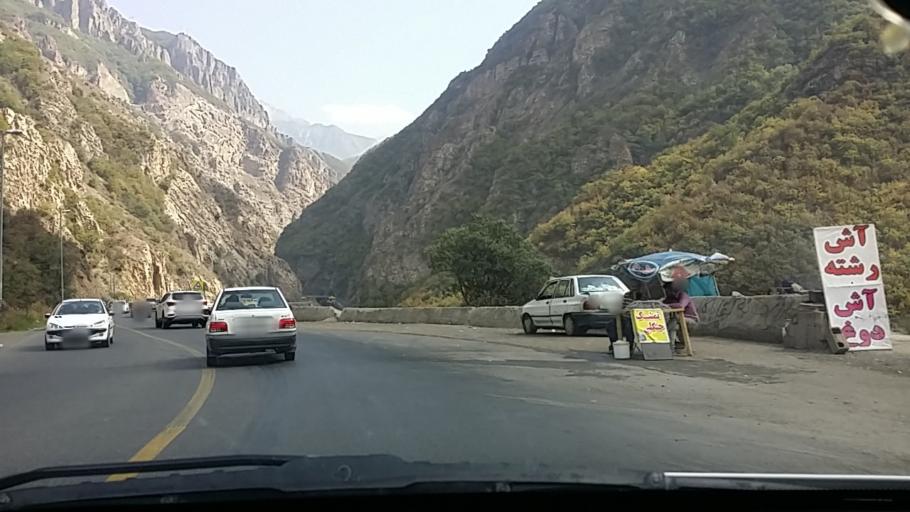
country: IR
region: Mazandaran
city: Chalus
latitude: 36.2664
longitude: 51.2591
